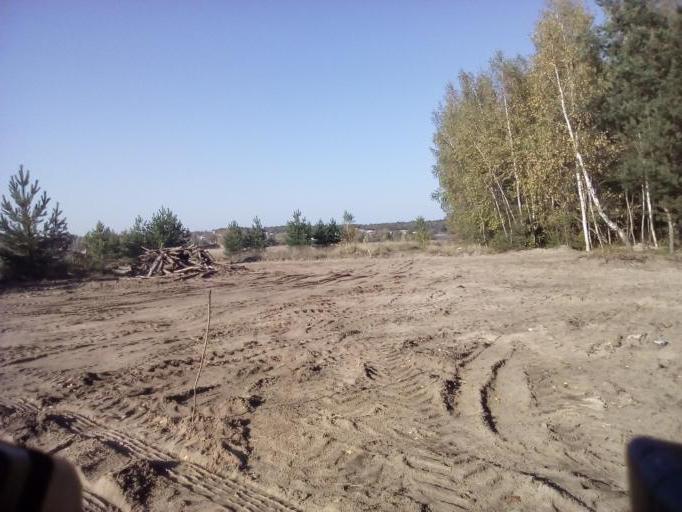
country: RU
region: Moskovskaya
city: Ramenskoye
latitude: 55.5704
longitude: 38.3056
